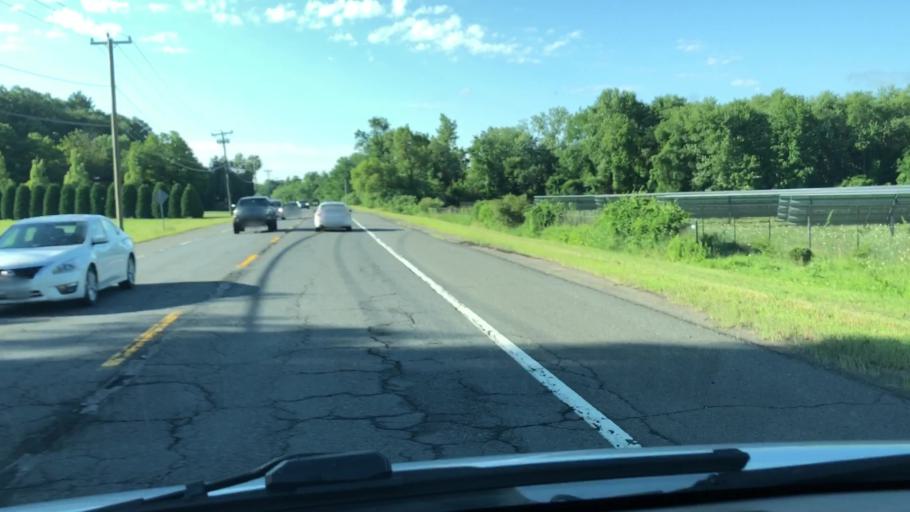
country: US
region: Massachusetts
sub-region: Franklin County
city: South Deerfield
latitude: 42.4628
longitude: -72.5734
